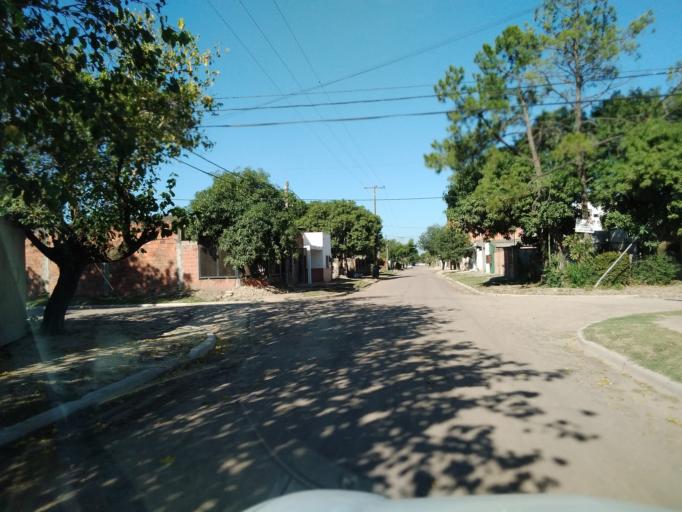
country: AR
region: Corrientes
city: Corrientes
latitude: -27.4836
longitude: -58.8116
